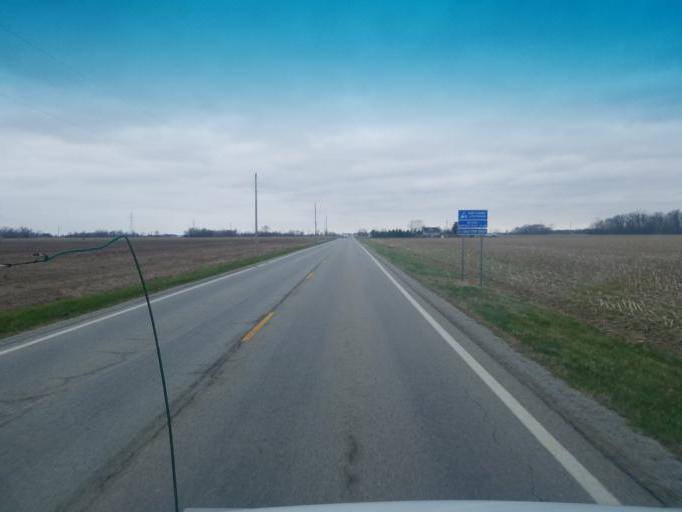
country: US
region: Ohio
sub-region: Allen County
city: Delphos
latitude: 40.9321
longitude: -84.4334
